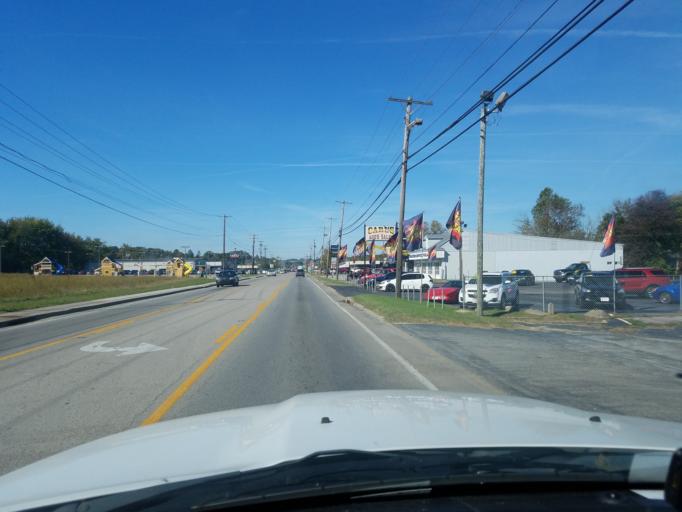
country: US
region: Kentucky
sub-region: Laurel County
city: London
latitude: 37.0985
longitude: -84.0679
